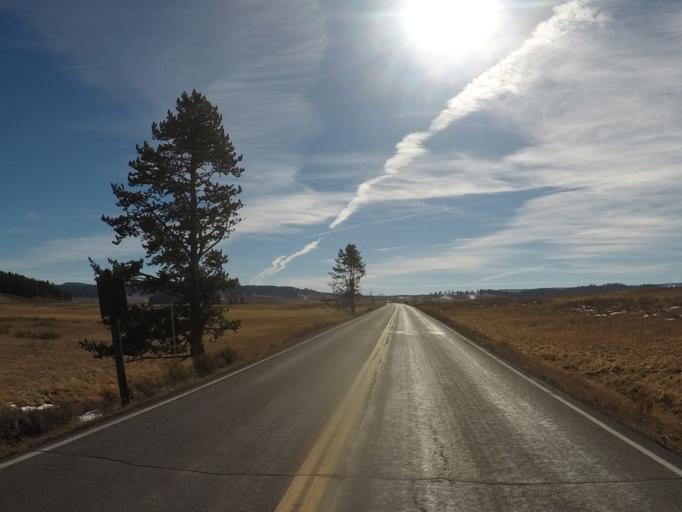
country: US
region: Montana
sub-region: Gallatin County
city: West Yellowstone
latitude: 44.6831
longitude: -110.4934
